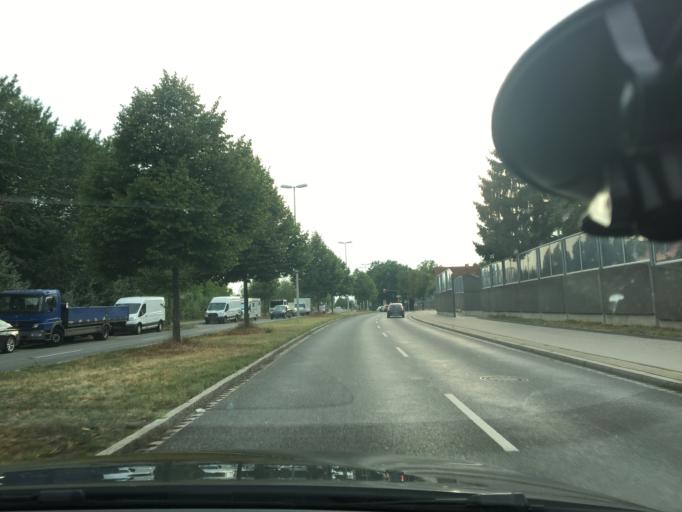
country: DE
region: Bavaria
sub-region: Regierungsbezirk Mittelfranken
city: Grossreuth bei Schweinau
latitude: 49.4415
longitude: 11.0259
